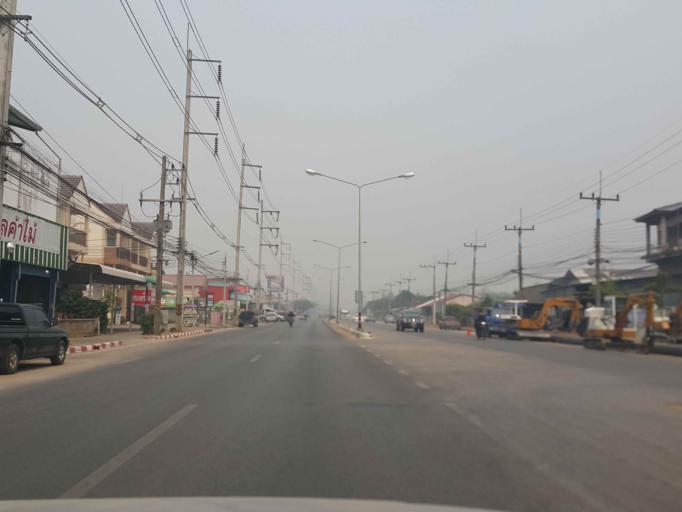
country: TH
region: Chiang Mai
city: Mae Taeng
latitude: 19.0992
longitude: 98.9357
